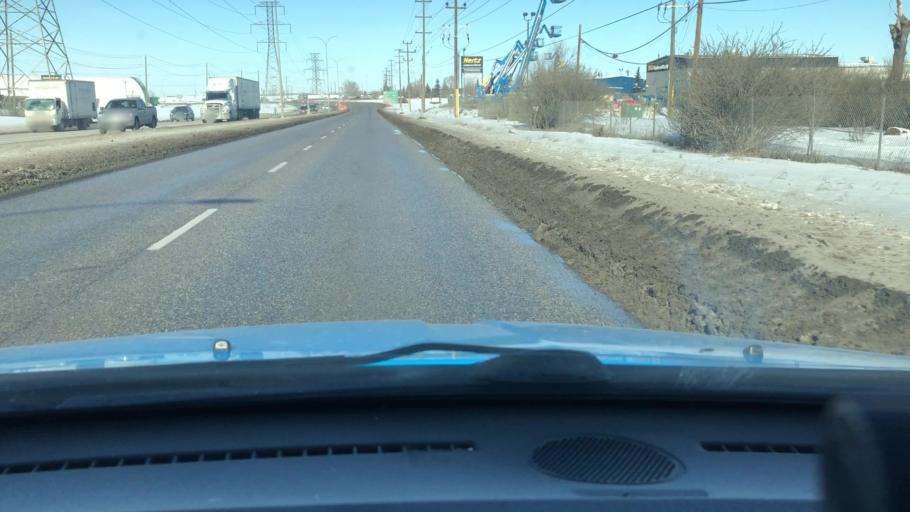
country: CA
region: Alberta
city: Calgary
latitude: 51.0107
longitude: -114.0017
